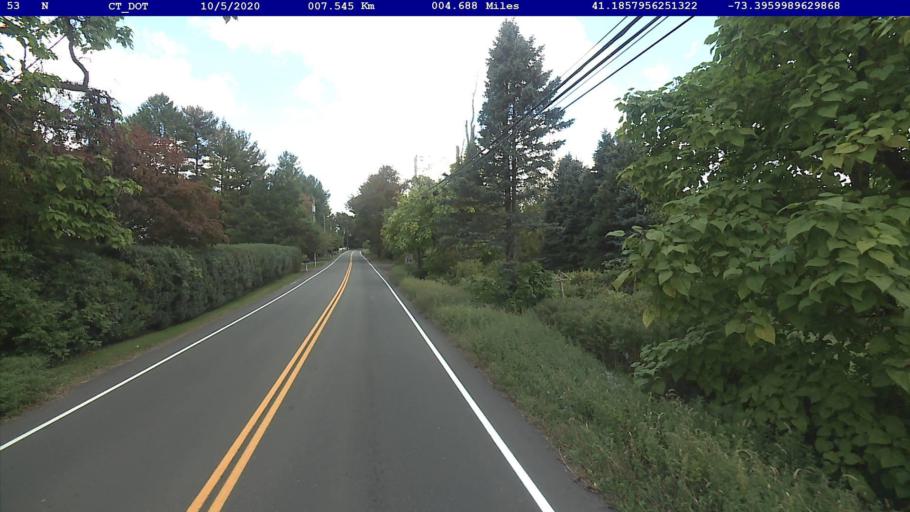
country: US
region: Connecticut
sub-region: Fairfield County
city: Wilton
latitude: 41.1858
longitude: -73.3960
